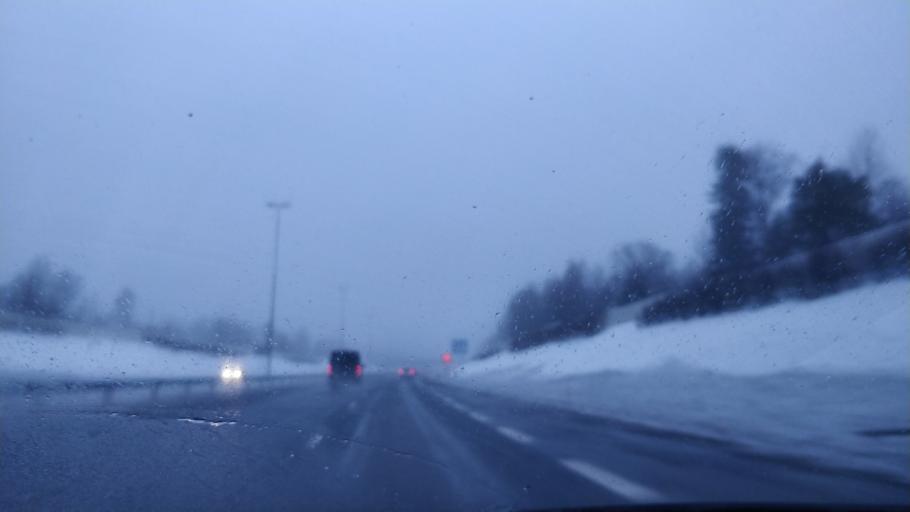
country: FI
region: Lapland
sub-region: Kemi-Tornio
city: Kemi
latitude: 65.7472
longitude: 24.5789
